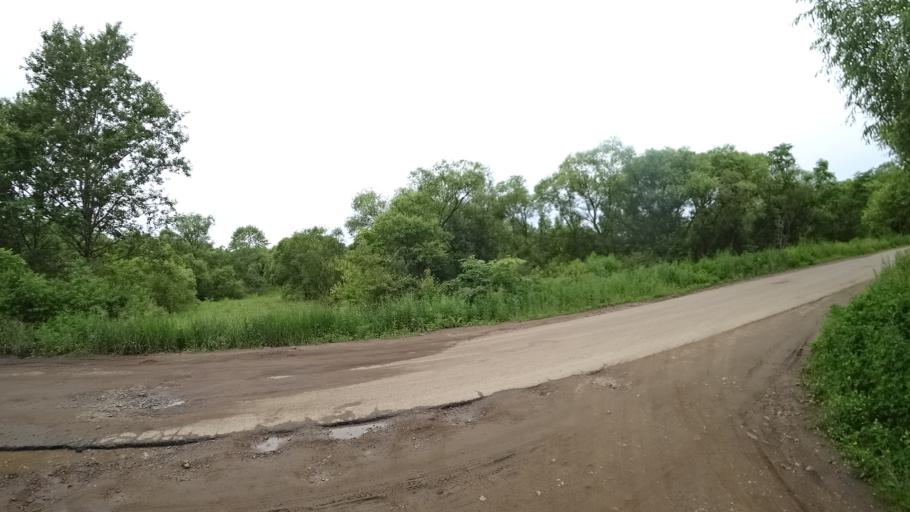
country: RU
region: Primorskiy
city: Novosysoyevka
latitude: 44.2045
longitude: 133.3259
